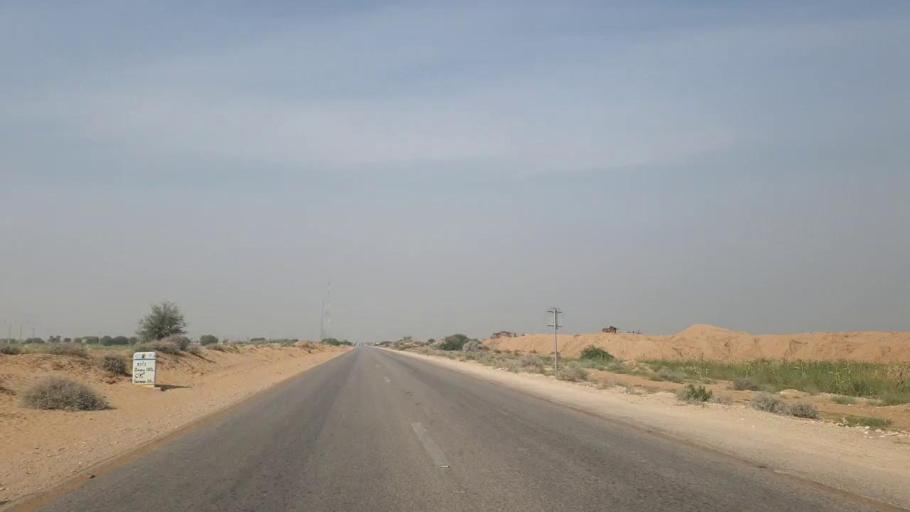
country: PK
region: Sindh
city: Sann
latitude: 26.0463
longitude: 68.1103
